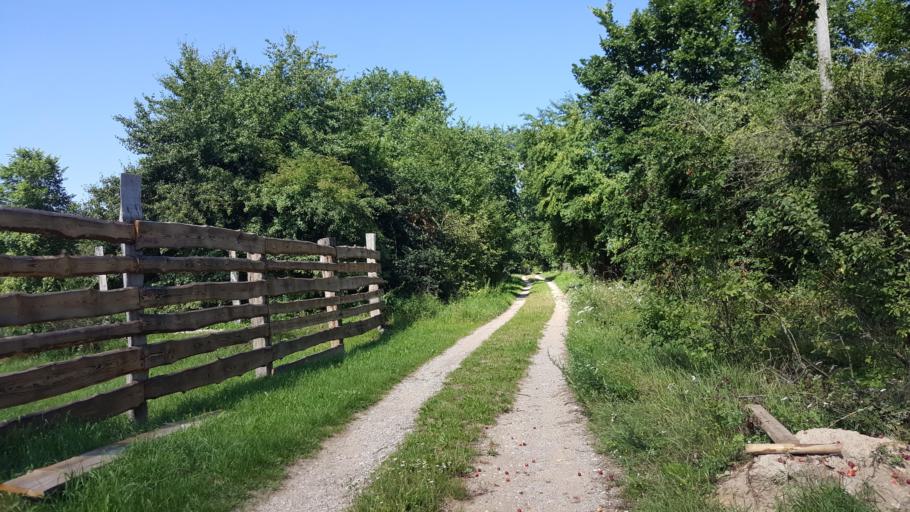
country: BY
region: Brest
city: Charnawchytsy
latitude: 52.3552
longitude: 23.6201
